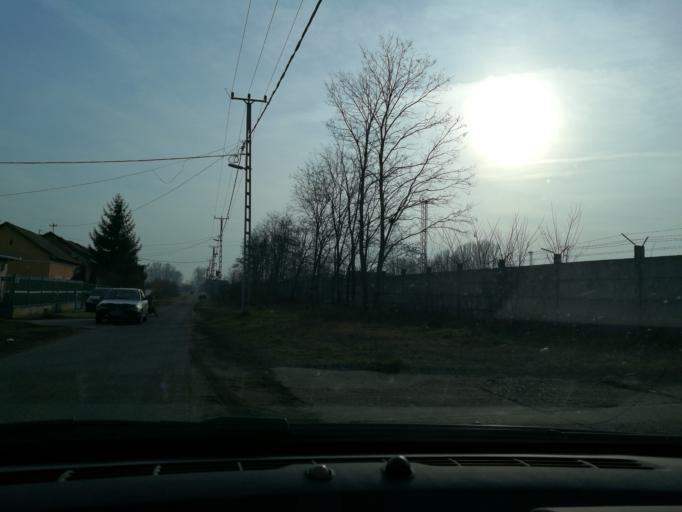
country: HU
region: Szabolcs-Szatmar-Bereg
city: Nyiregyhaza
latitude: 47.9380
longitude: 21.7004
